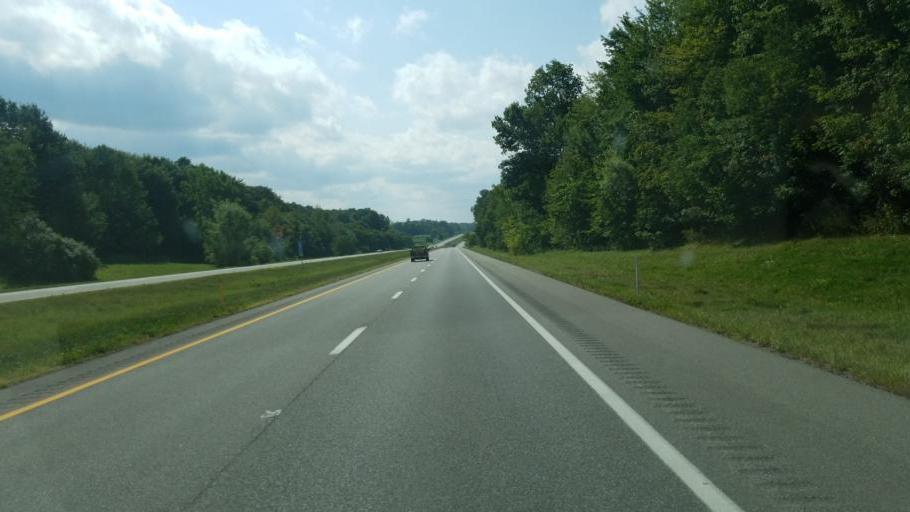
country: US
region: Ohio
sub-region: Geauga County
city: Bainbridge
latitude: 41.3826
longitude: -81.2569
